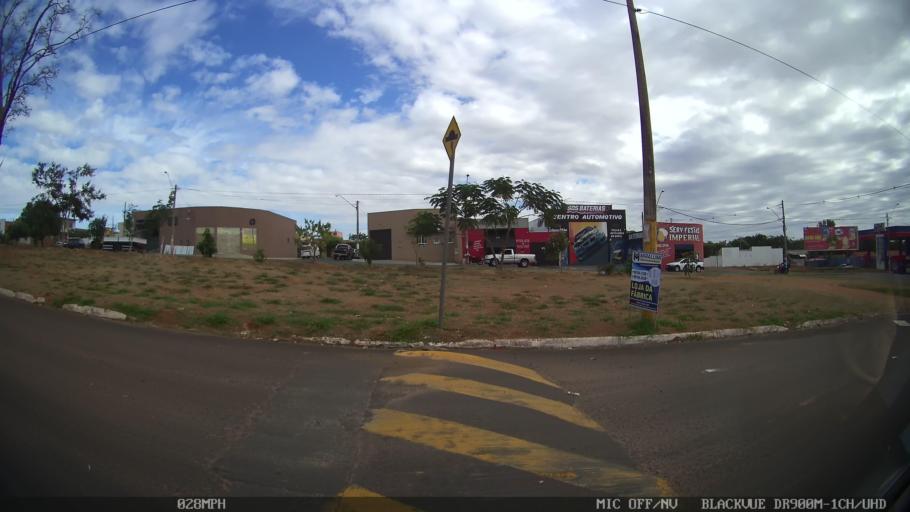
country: BR
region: Sao Paulo
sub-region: Sao Jose Do Rio Preto
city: Sao Jose do Rio Preto
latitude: -20.8031
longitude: -49.5049
